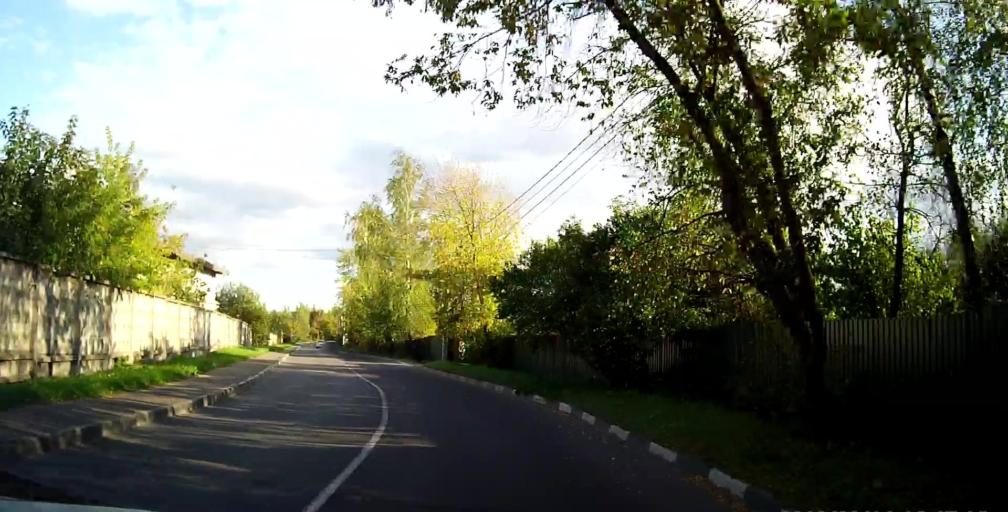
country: RU
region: Moskovskaya
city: Klimovsk
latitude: 55.3663
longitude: 37.5479
